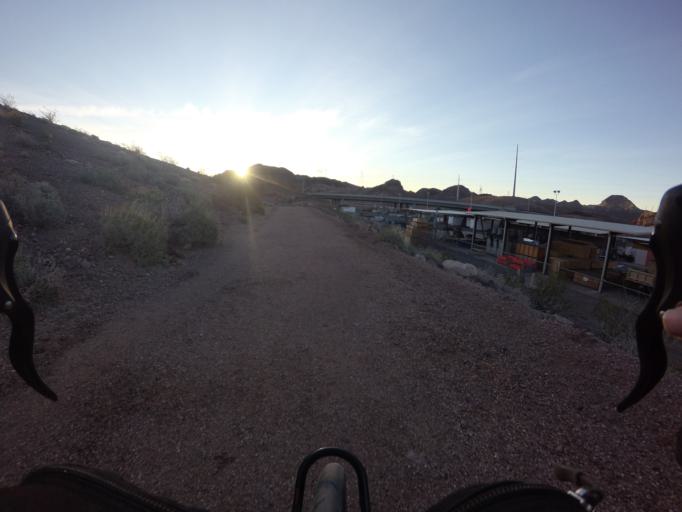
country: US
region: Nevada
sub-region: Clark County
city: Boulder City
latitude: 36.0161
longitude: -114.7572
